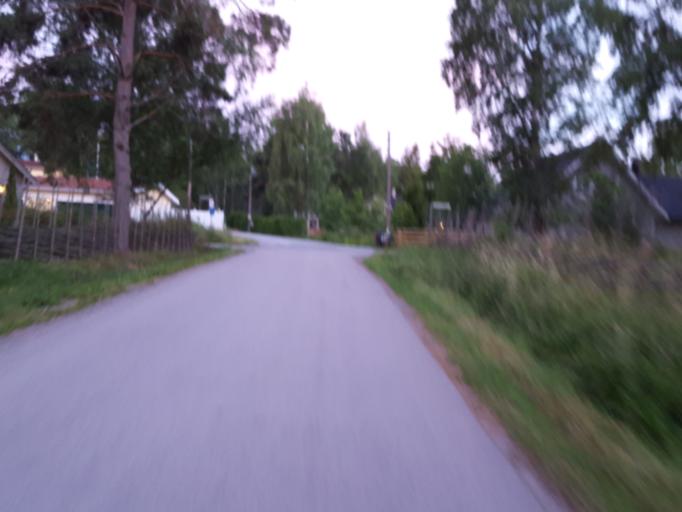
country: SE
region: Uppsala
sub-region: Uppsala Kommun
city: Uppsala
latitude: 59.7791
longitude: 17.6037
